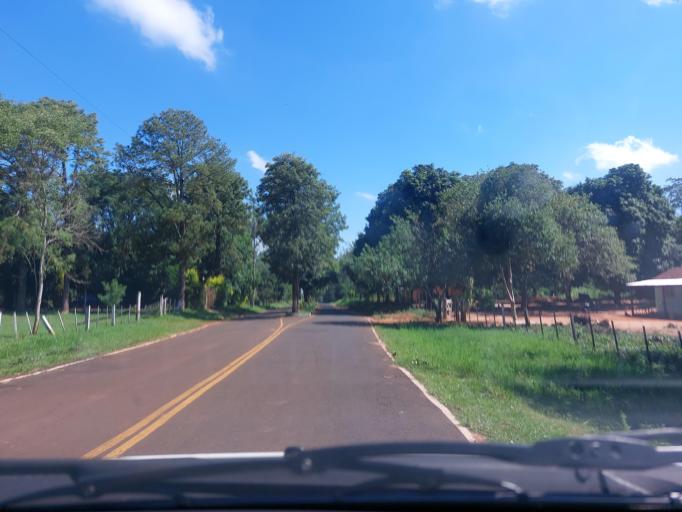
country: PY
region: San Pedro
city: Guayaybi
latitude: -24.5313
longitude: -56.5577
